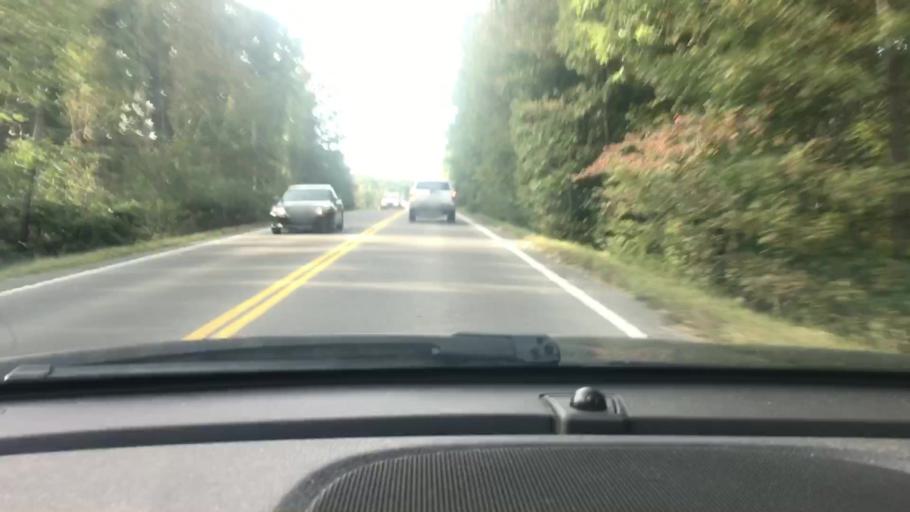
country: US
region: Tennessee
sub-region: Williamson County
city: Fairview
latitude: 35.9874
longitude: -87.1196
